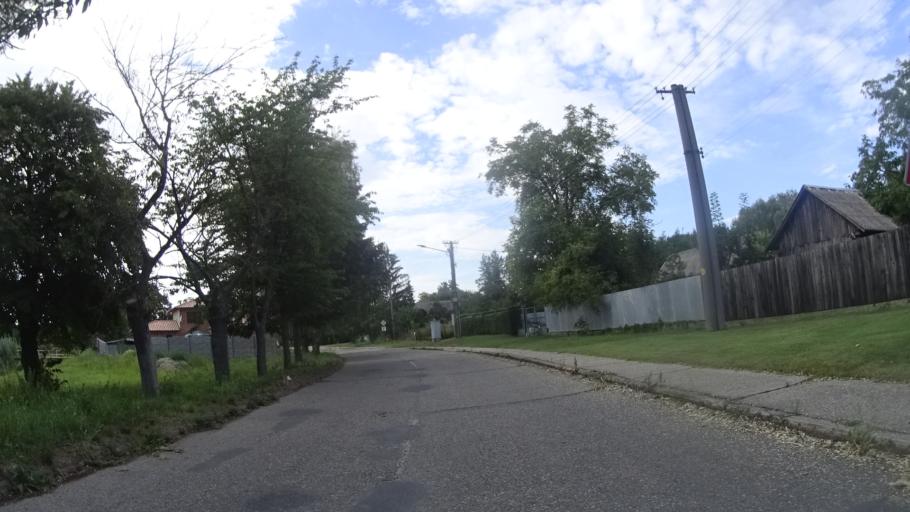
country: SK
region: Trnavsky
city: Gabcikovo
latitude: 47.9046
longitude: 17.5262
